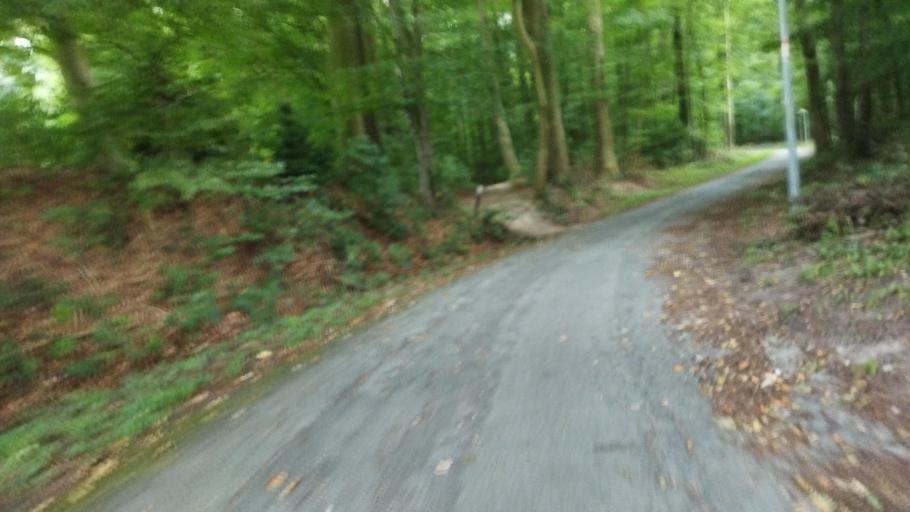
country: DE
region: Lower Saxony
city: Bad Iburg
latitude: 52.1656
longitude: 8.0305
